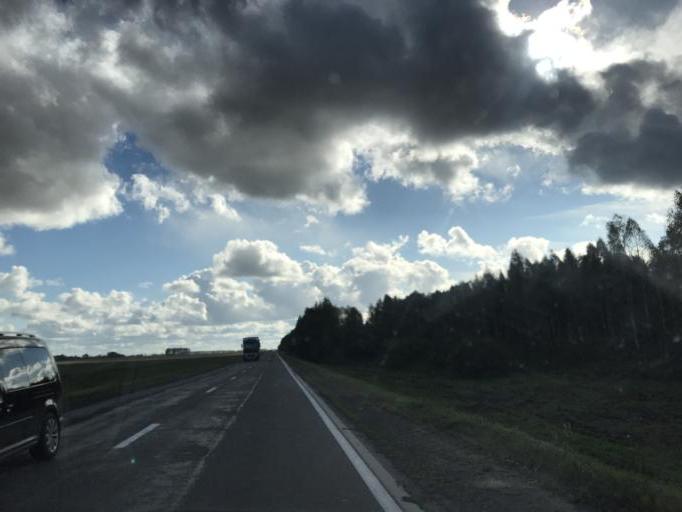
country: BY
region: Gomel
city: Buda-Kashalyova
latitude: 52.8443
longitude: 30.7028
